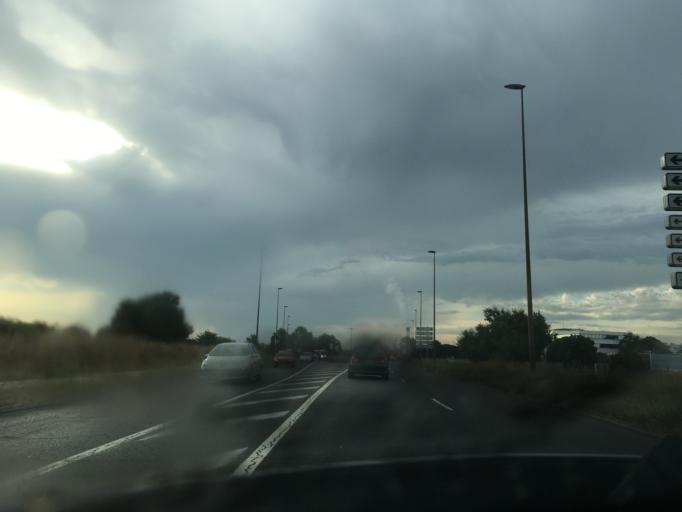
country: FR
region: Midi-Pyrenees
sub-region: Departement de la Haute-Garonne
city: Portet-sur-Garonne
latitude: 43.5631
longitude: 1.3879
